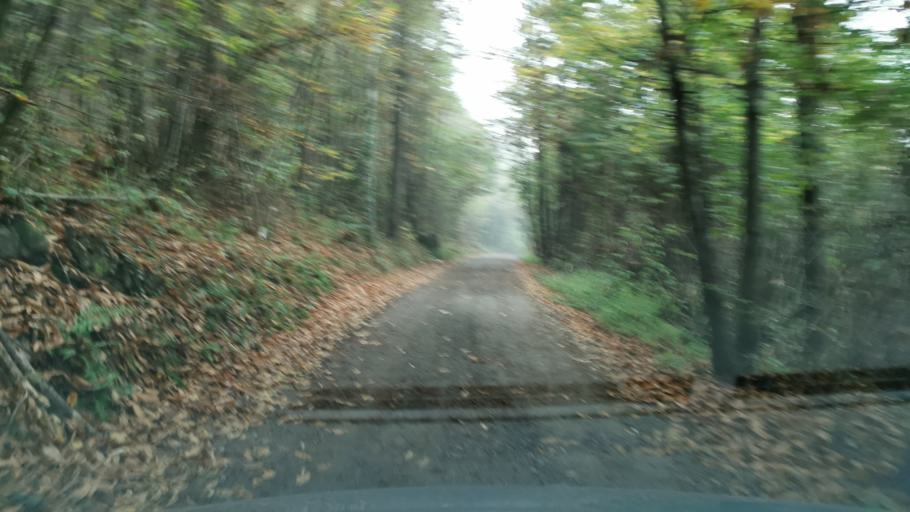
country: IT
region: Piedmont
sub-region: Provincia di Torino
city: Scarmagno
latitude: 45.3835
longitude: 7.8345
